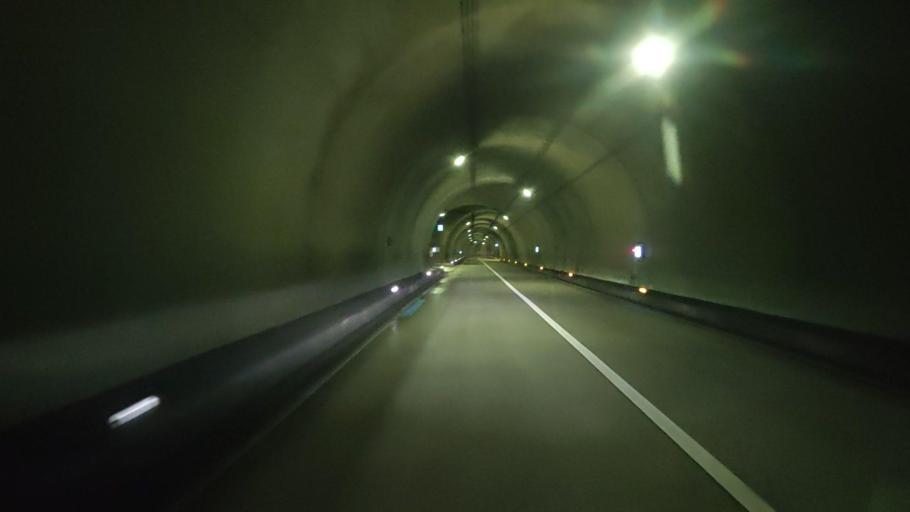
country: JP
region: Wakayama
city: Shingu
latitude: 33.8550
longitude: 135.8533
